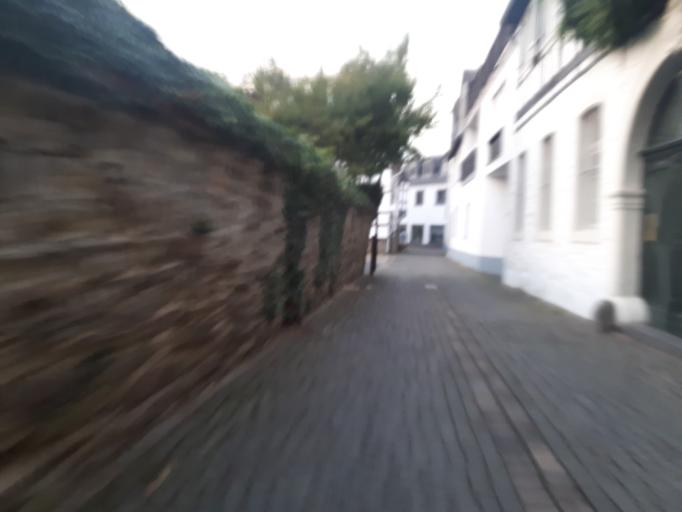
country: DE
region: Rheinland-Pfalz
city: Unkel
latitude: 50.5984
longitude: 7.2153
